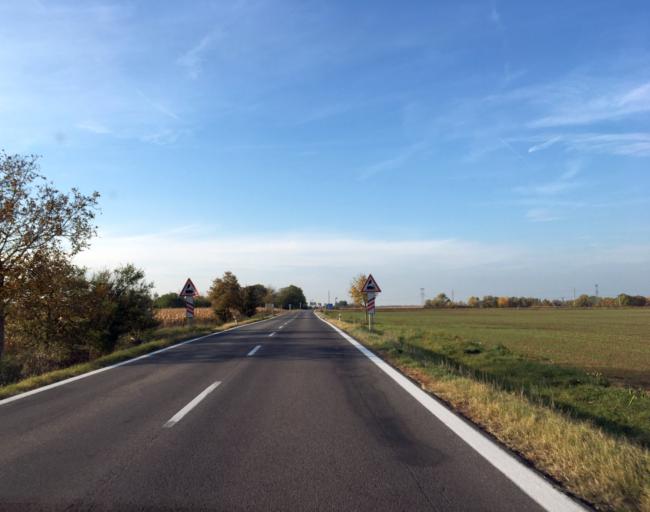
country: SK
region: Nitriansky
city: Surany
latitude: 48.0576
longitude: 18.1039
